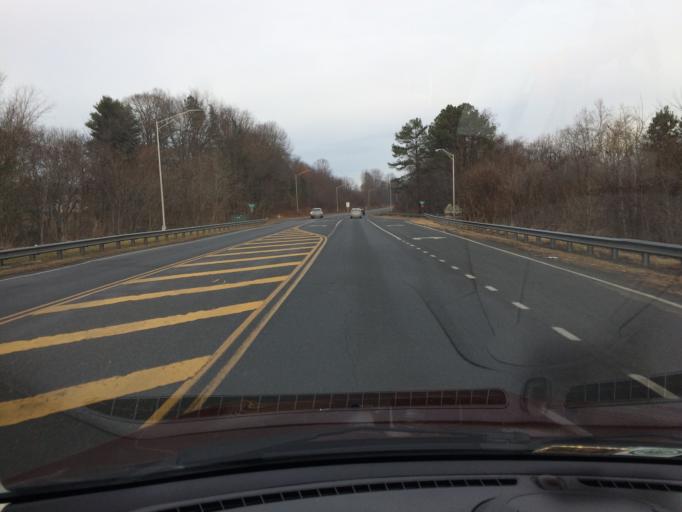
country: US
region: Virginia
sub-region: City of Bedford
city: Bedford
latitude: 37.3421
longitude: -79.5004
